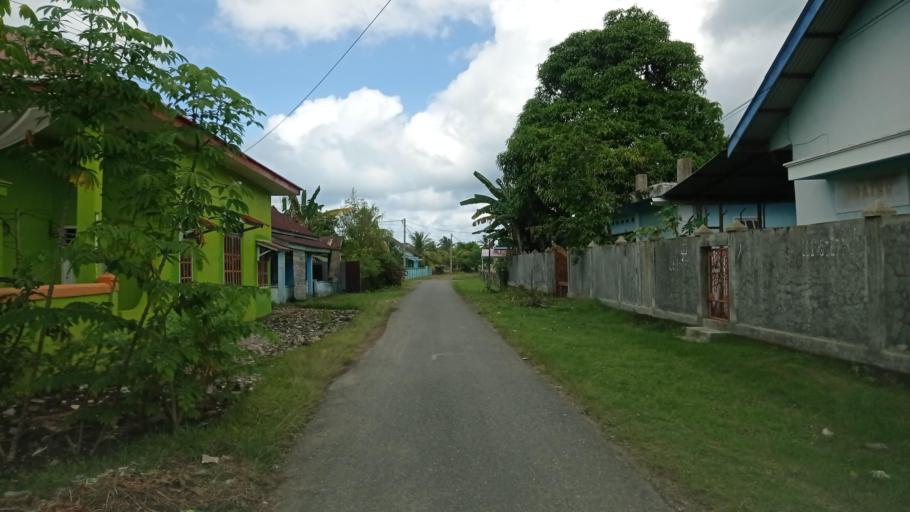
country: ID
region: Jambi
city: Sungai Penuh
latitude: -2.5571
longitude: 101.1035
